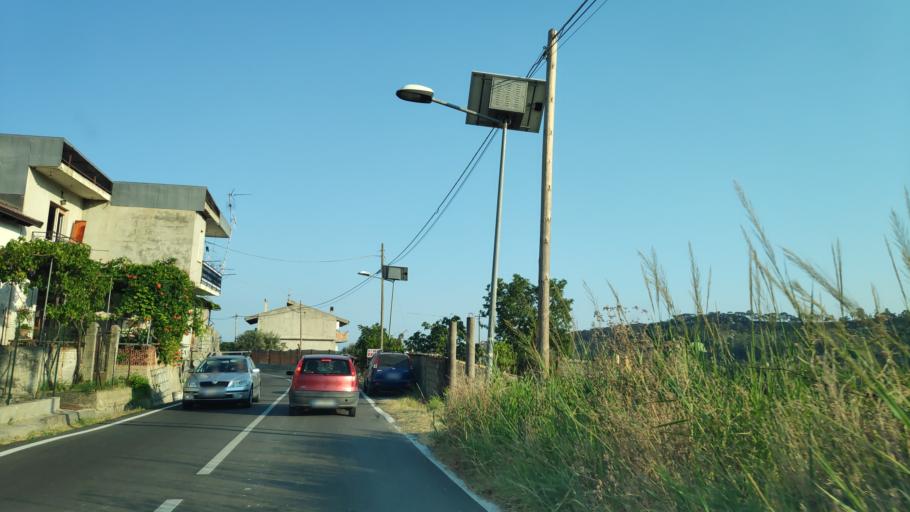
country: IT
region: Calabria
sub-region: Provincia di Reggio Calabria
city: Caulonia Marina
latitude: 38.3683
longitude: 16.4485
